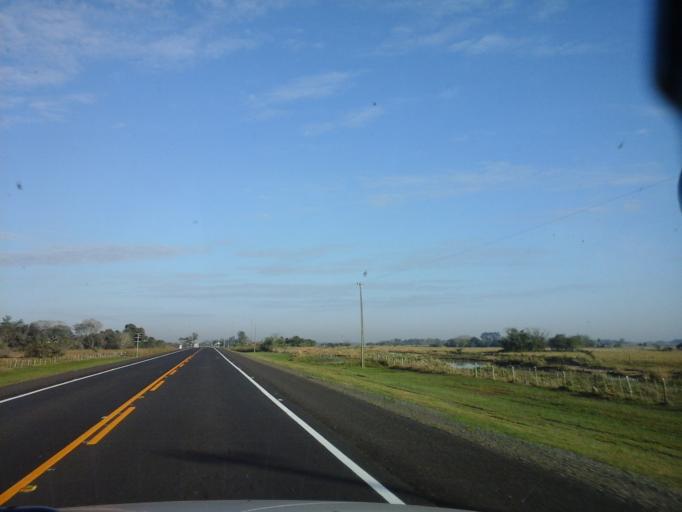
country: PY
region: Neembucu
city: Cerrito
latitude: -26.8663
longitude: -57.5775
